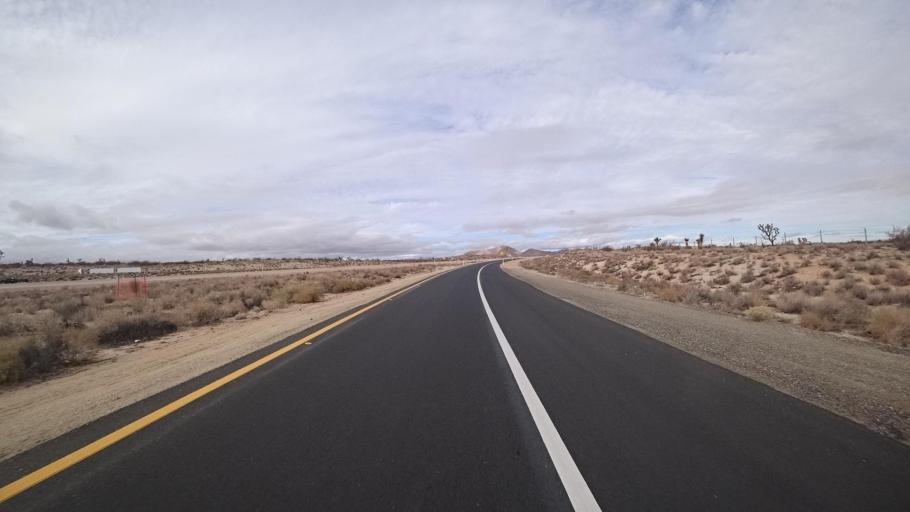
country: US
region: California
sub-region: Kern County
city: Rosamond
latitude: 34.9095
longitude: -118.1630
